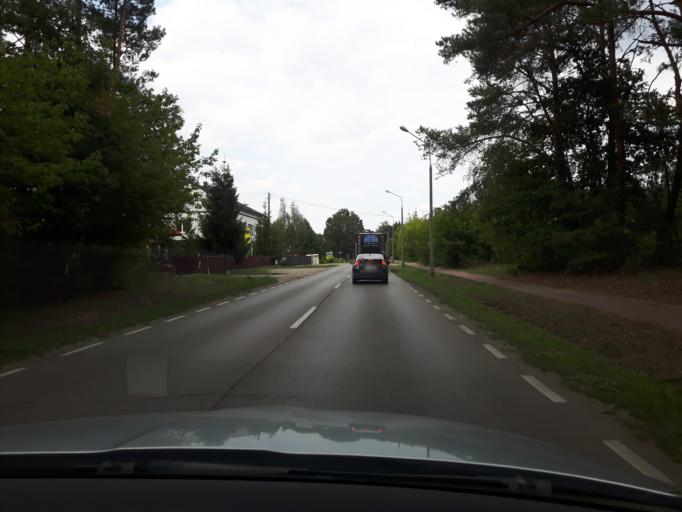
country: PL
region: Masovian Voivodeship
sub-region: Powiat legionowski
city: Stanislawow Pierwszy
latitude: 52.3865
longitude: 21.0306
